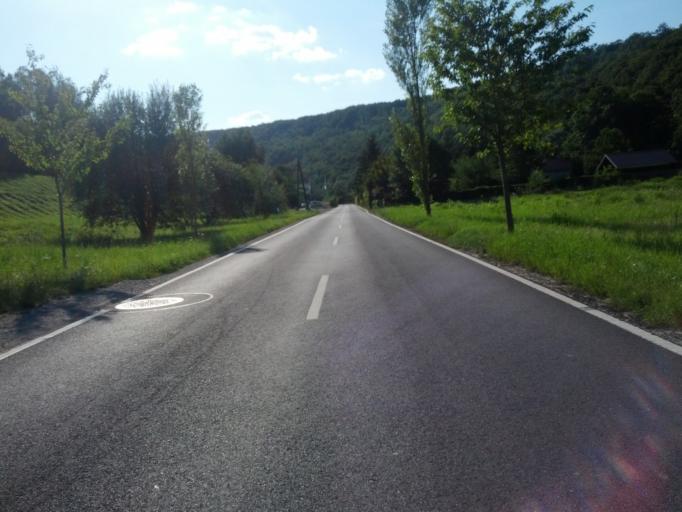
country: DE
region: Thuringia
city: Ebenshausen
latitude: 51.0730
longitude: 10.2820
